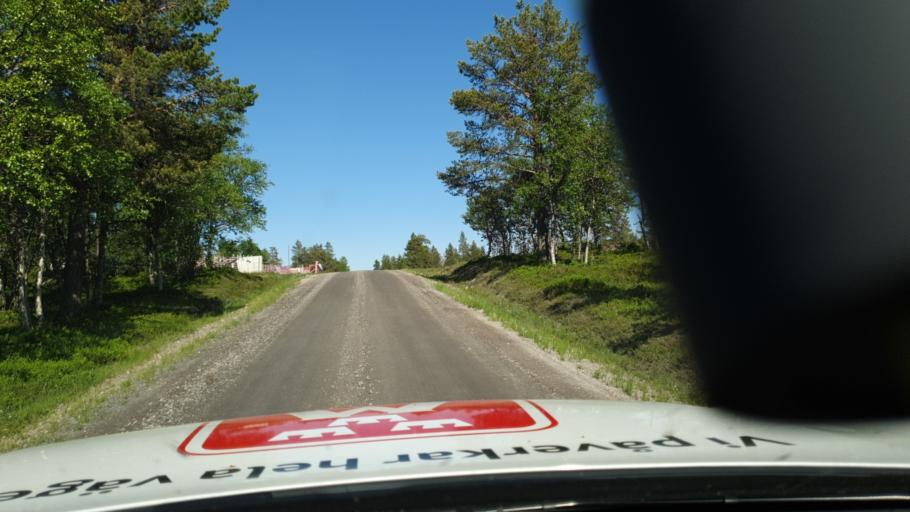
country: NO
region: Hedmark
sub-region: Engerdal
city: Engerdal
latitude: 62.1378
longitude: 12.9339
